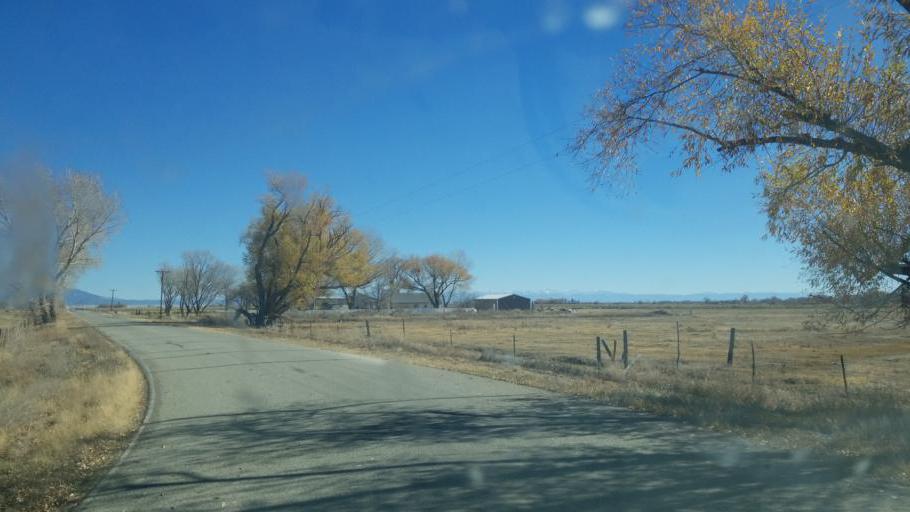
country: US
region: Colorado
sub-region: Alamosa County
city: Alamosa
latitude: 37.5306
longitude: -105.9288
